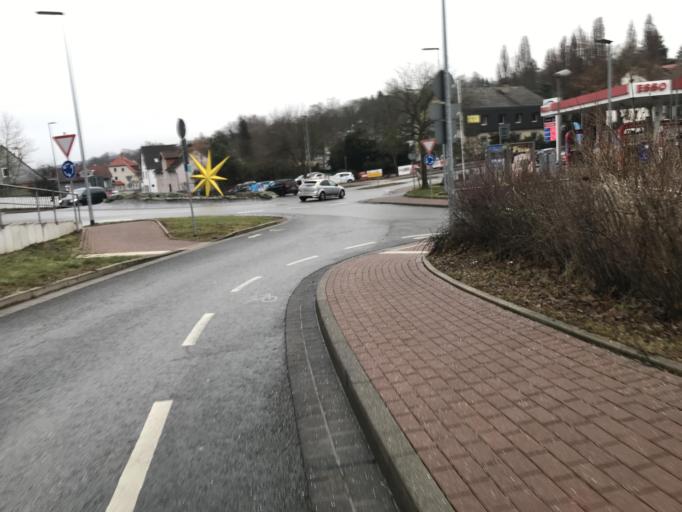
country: DE
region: Hesse
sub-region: Regierungsbezirk Kassel
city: Bad Wildungen
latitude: 51.1177
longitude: 9.1237
